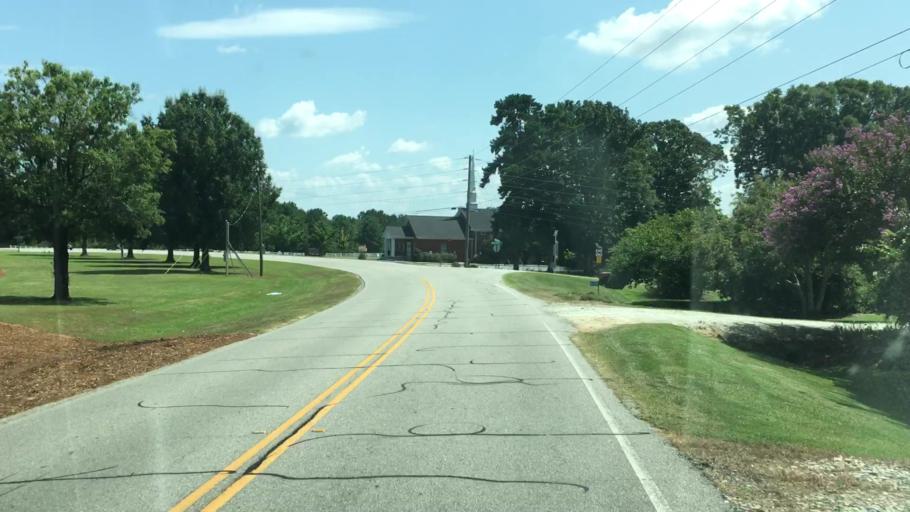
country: US
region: Georgia
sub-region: Oconee County
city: Watkinsville
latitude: 33.8607
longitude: -83.4581
